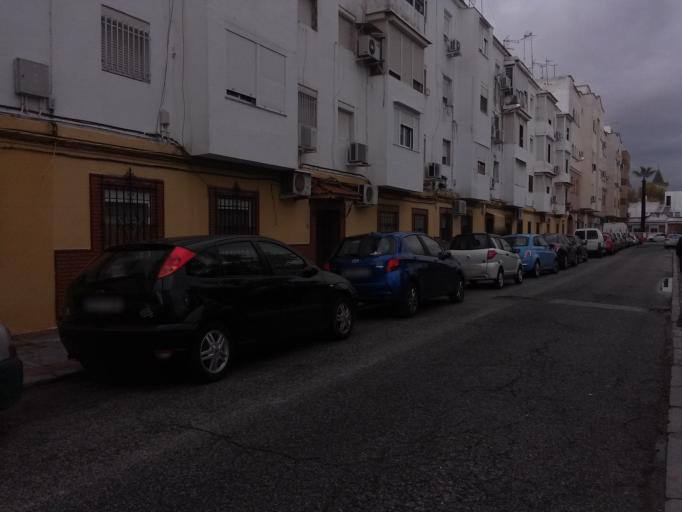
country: ES
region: Andalusia
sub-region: Provincia de Sevilla
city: Sevilla
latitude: 37.4261
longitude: -5.9837
